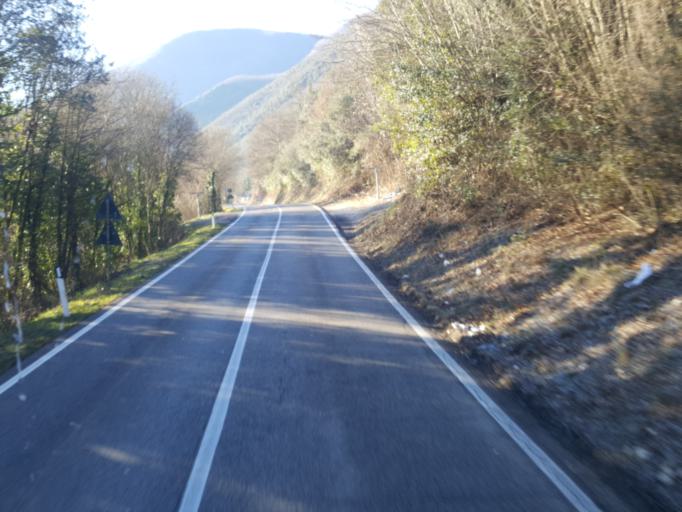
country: IT
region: Latium
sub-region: Provincia di Rieti
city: Colli sul Velino
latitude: 42.5117
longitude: 12.7396
